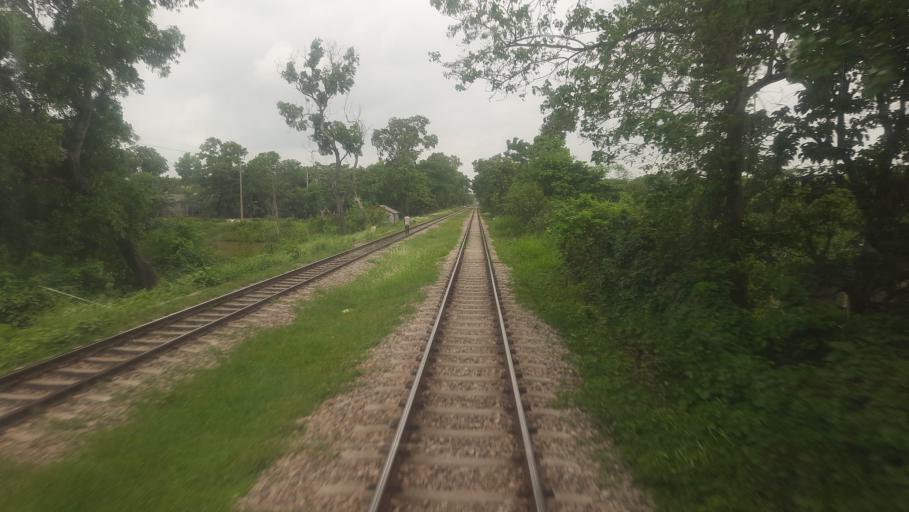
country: BD
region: Dhaka
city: Bhairab Bazar
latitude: 23.9754
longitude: 91.0841
